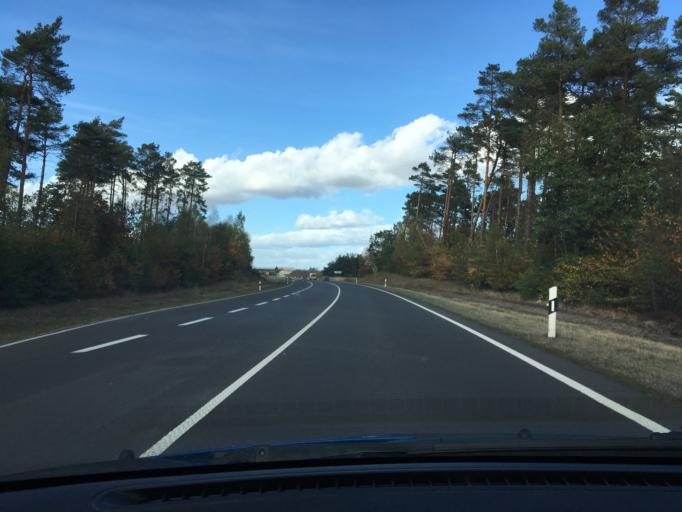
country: DE
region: Brandenburg
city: Perleberg
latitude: 53.0582
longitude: 11.8326
